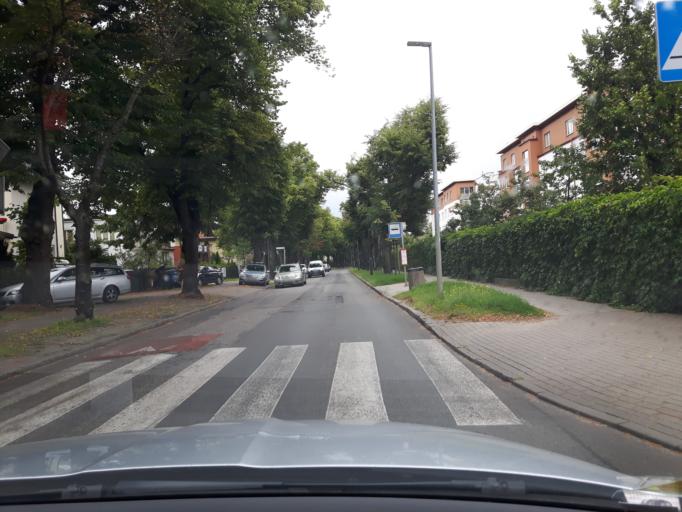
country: PL
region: Pomeranian Voivodeship
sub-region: Sopot
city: Sopot
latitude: 54.4144
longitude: 18.5798
